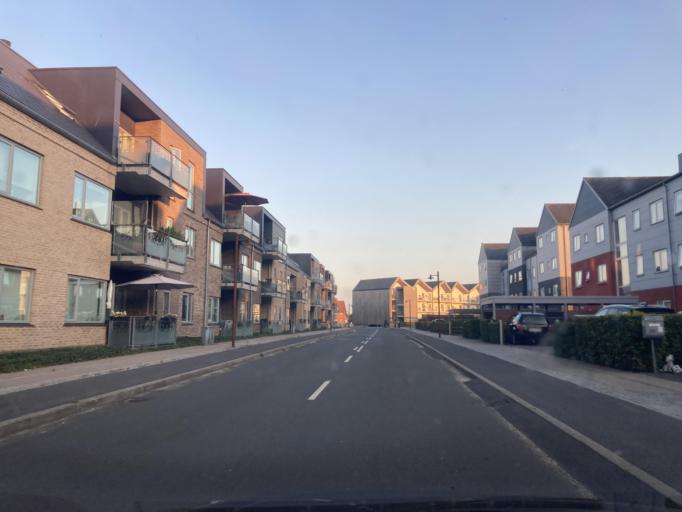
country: DK
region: South Denmark
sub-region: Nyborg Kommune
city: Nyborg
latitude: 55.3080
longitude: 10.7953
